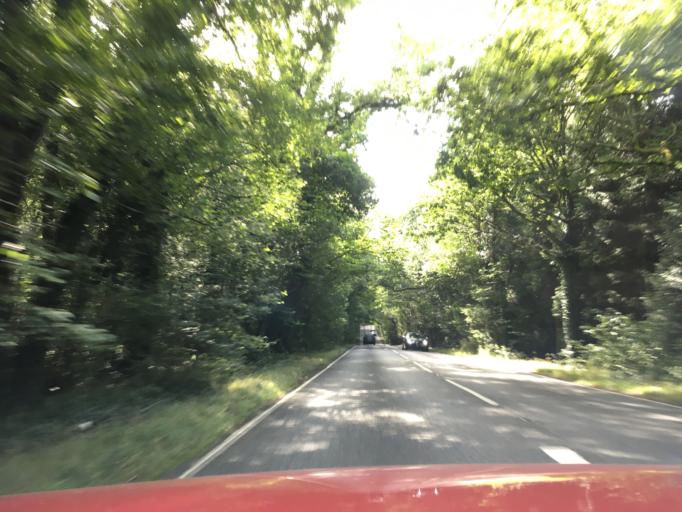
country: GB
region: England
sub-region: West Sussex
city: Billingshurst
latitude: 51.0524
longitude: -0.4084
